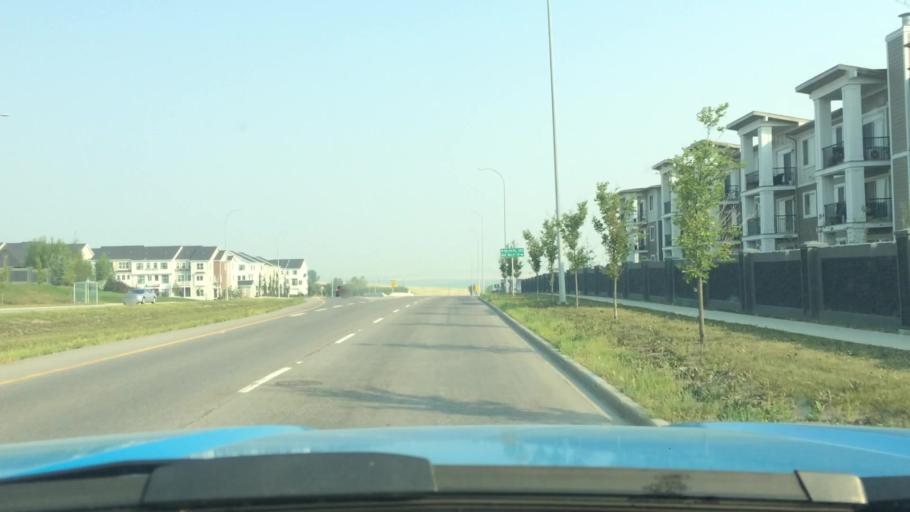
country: CA
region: Alberta
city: Calgary
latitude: 51.1787
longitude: -114.1590
